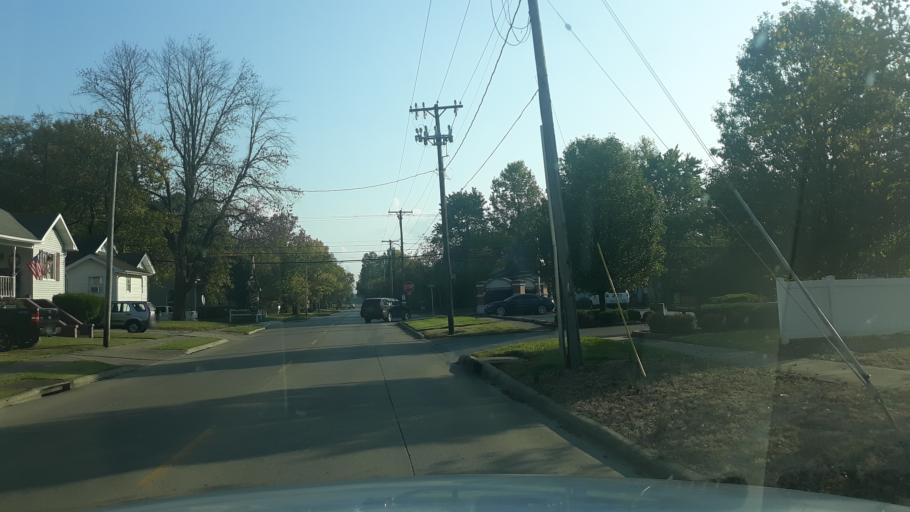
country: US
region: Illinois
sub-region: Saline County
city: Harrisburg
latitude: 37.7318
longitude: -88.5403
